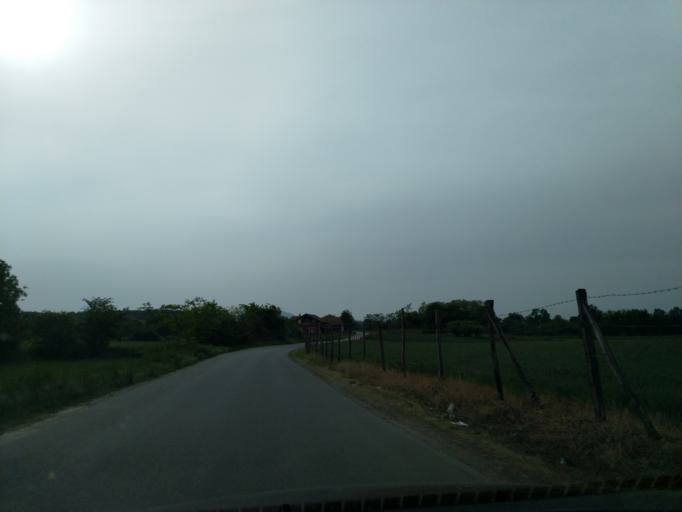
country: RS
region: Central Serbia
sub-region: Pomoravski Okrug
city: Jagodina
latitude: 43.9717
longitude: 21.2187
